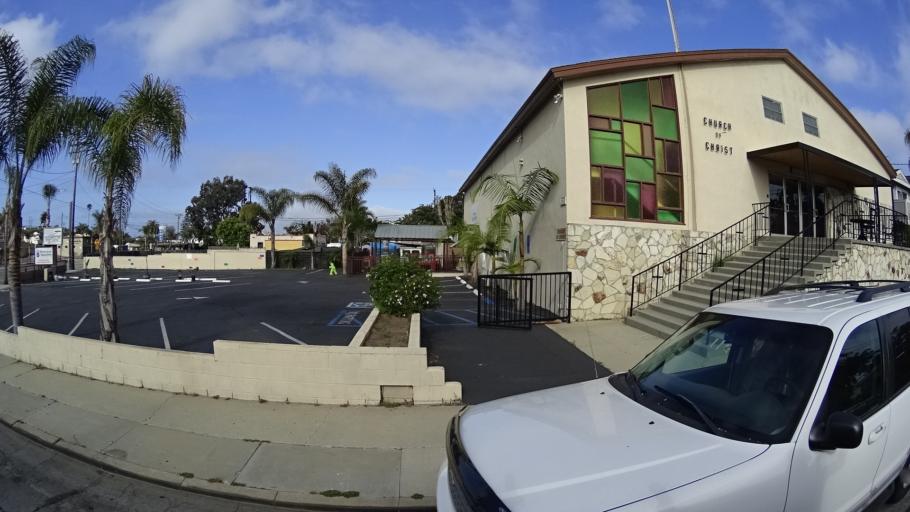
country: US
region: California
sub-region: Los Angeles County
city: Hermosa Beach
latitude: 33.8644
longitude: -118.3886
